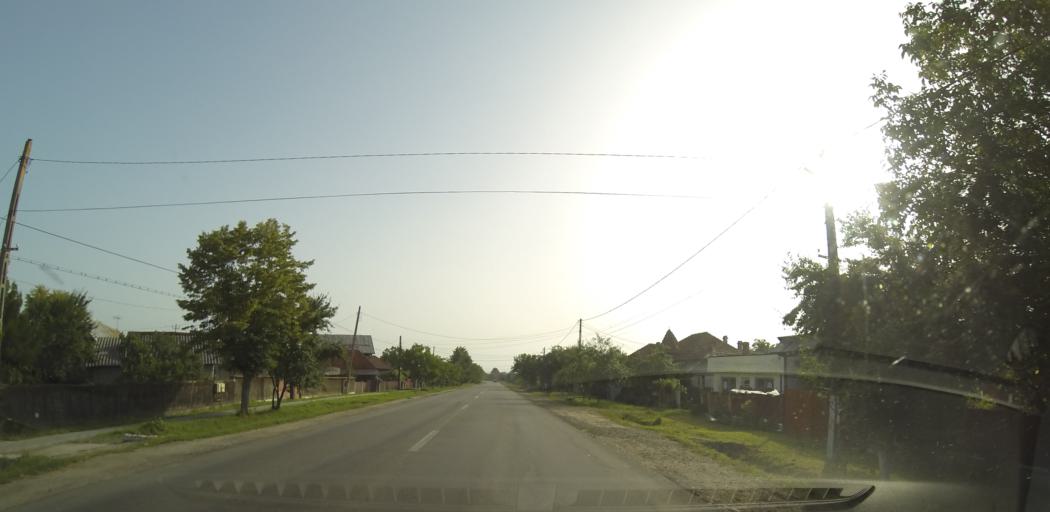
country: RO
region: Valcea
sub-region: Comuna Babeni
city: Babeni
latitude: 44.9838
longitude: 24.2500
